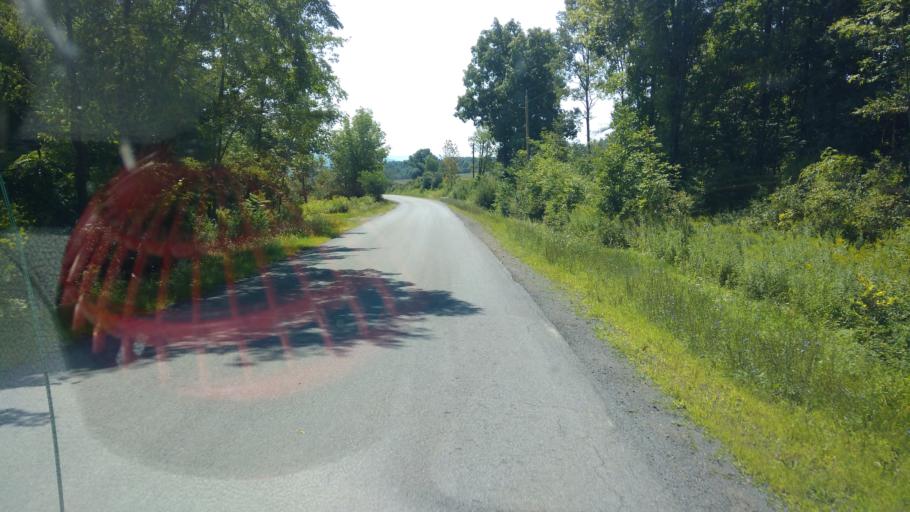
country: US
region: New York
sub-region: Allegany County
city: Belmont
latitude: 42.3426
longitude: -78.0417
